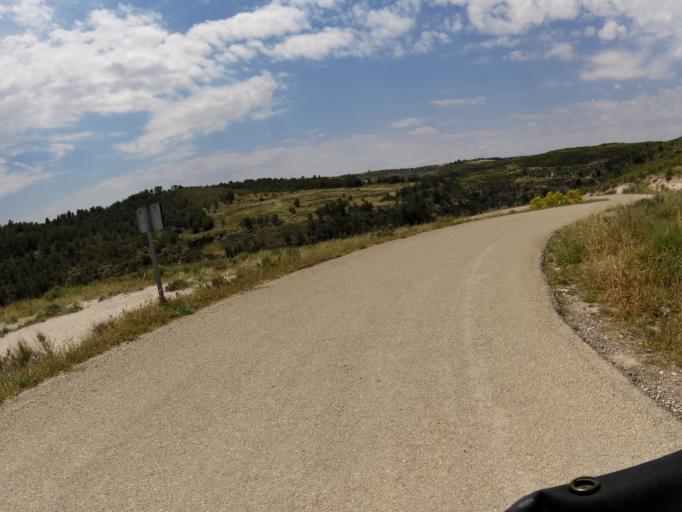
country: ES
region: Castille-La Mancha
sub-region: Provincia de Albacete
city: Valdeganga
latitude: 39.1614
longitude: -1.6135
